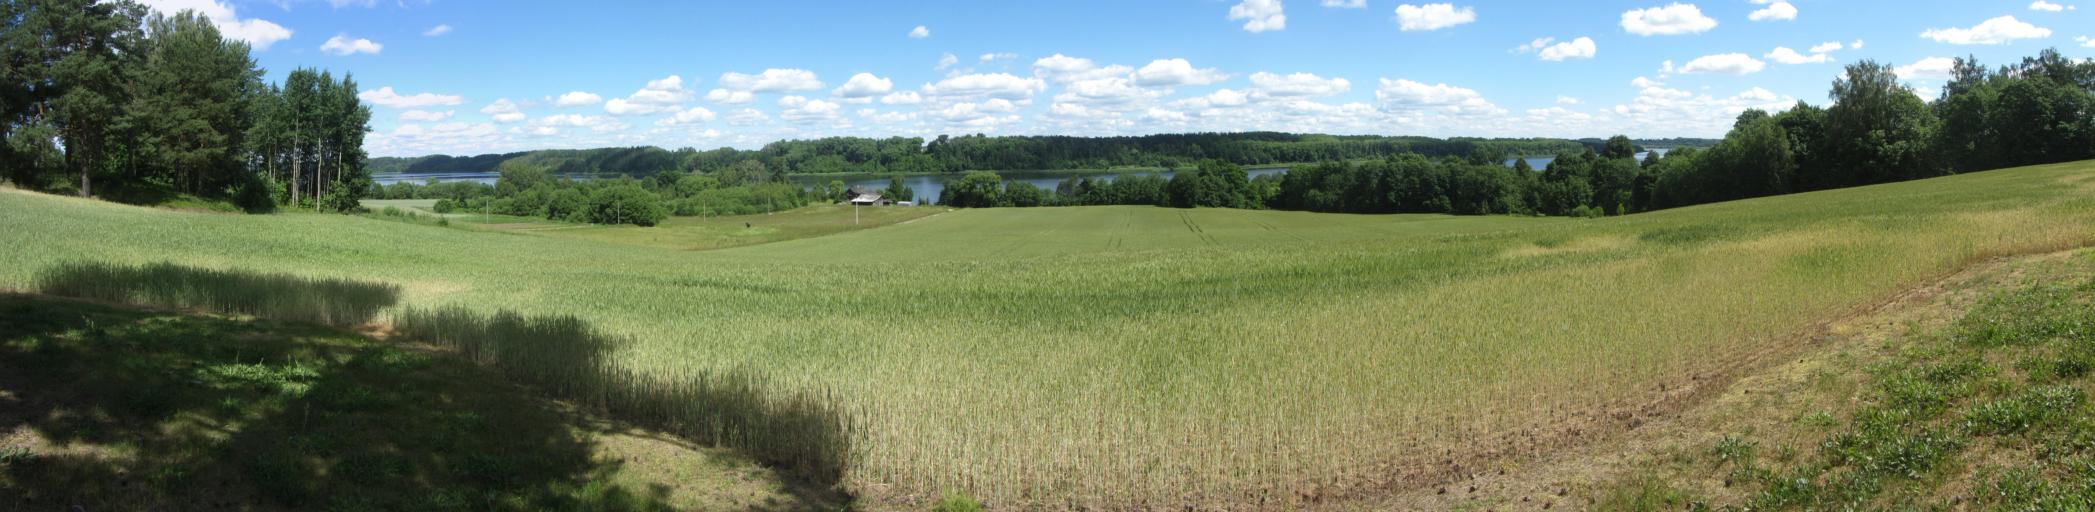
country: LT
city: Jieznas
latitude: 54.7992
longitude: 24.1905
